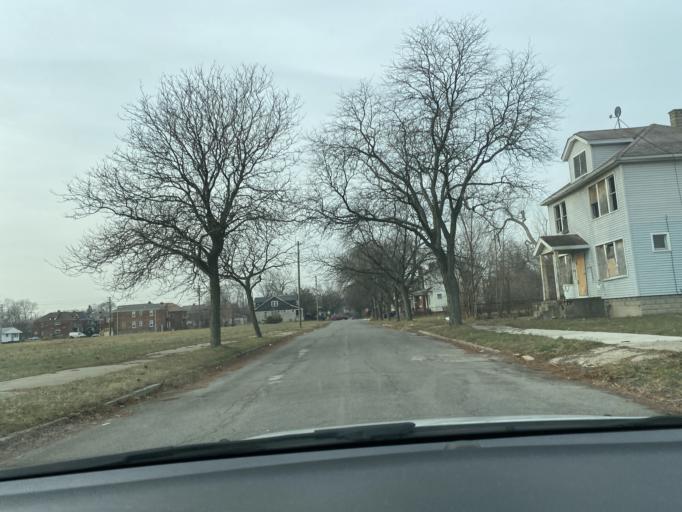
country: US
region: Michigan
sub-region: Wayne County
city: Highland Park
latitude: 42.3818
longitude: -83.1292
